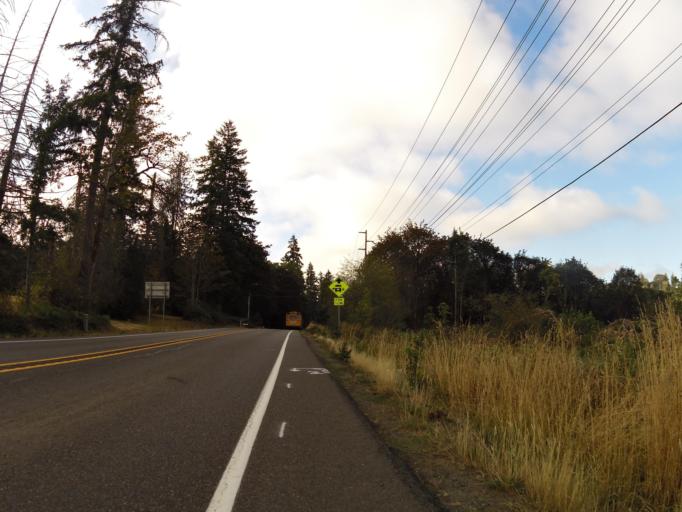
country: US
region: Washington
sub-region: Mason County
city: Belfair
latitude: 47.4265
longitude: -122.8455
